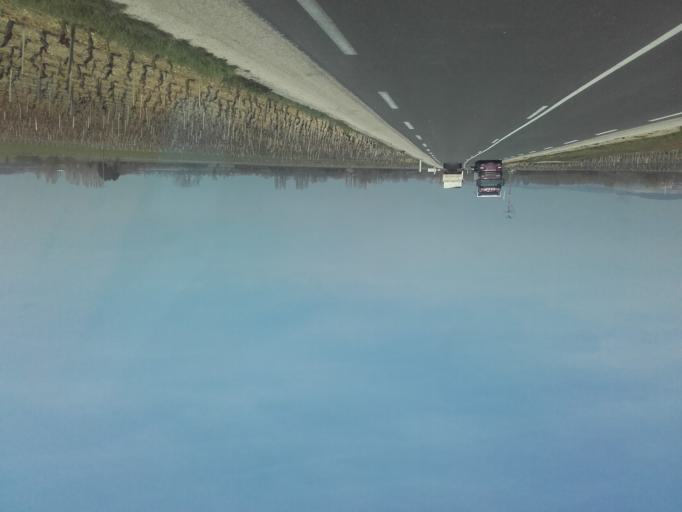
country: FR
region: Bourgogne
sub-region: Departement de la Cote-d'Or
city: Meursault
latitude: 46.9530
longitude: 4.7654
